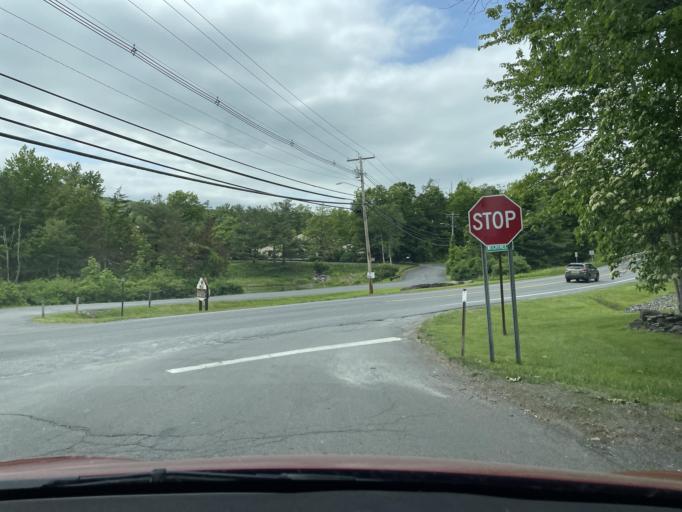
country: US
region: New York
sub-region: Ulster County
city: Woodstock
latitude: 42.0210
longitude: -74.1053
